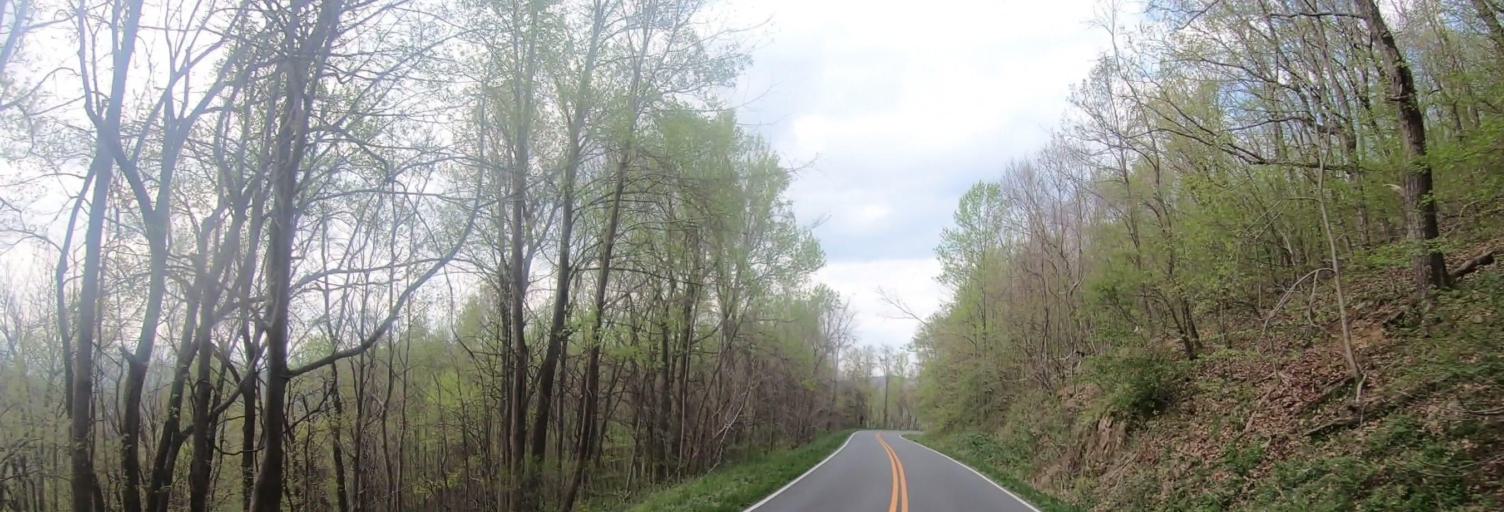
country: US
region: Virginia
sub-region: Augusta County
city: Dooms
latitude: 38.0825
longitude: -78.7939
